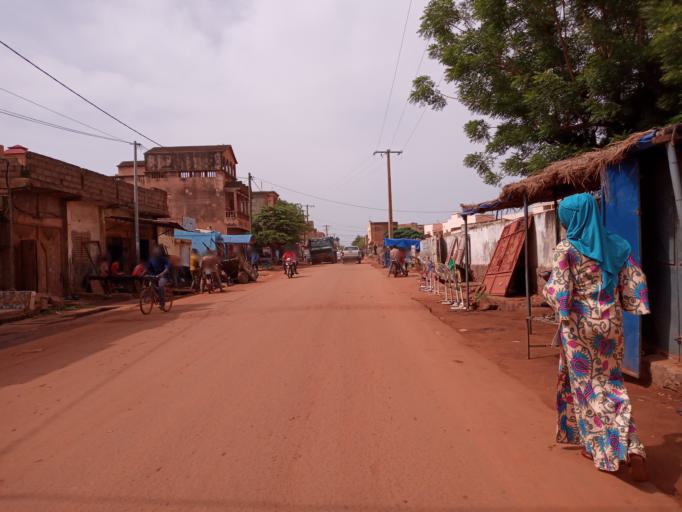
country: ML
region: Bamako
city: Bamako
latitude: 12.5559
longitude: -7.9904
